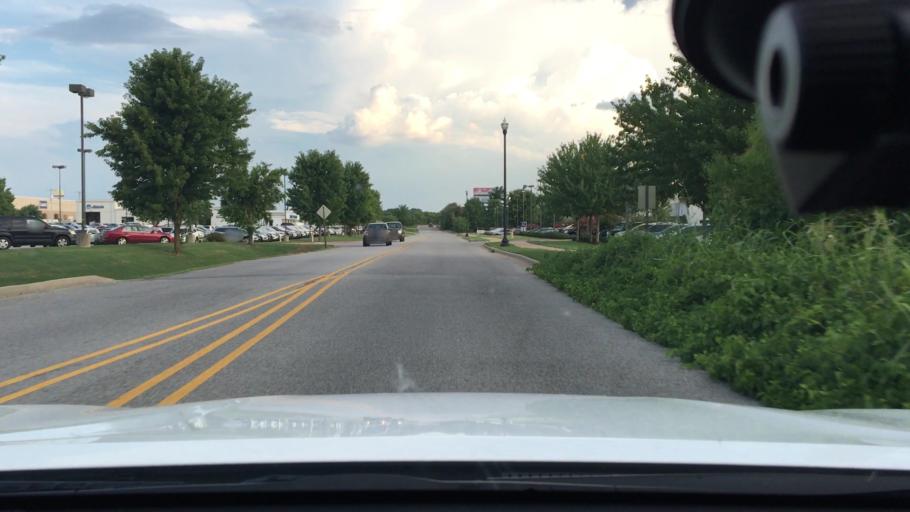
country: US
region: Arkansas
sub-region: Benton County
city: Bentonville
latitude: 36.3409
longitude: -94.1839
